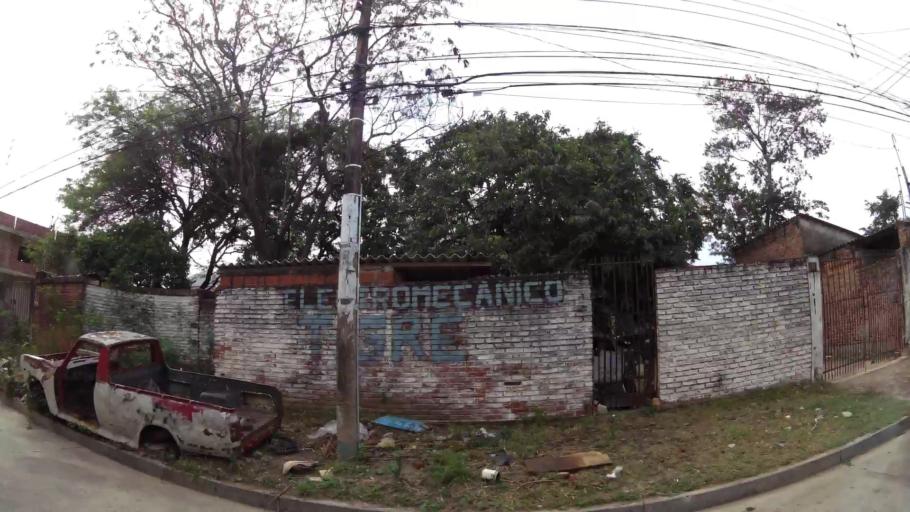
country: BO
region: Santa Cruz
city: Santa Cruz de la Sierra
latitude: -17.7801
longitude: -63.2158
